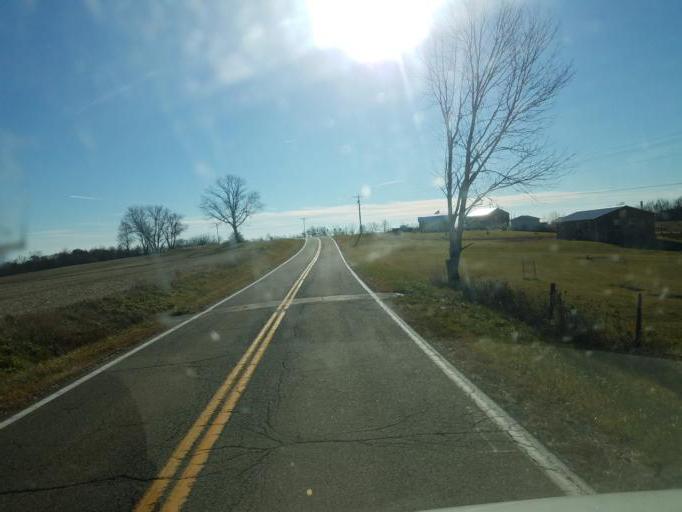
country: US
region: Ohio
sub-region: Knox County
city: Oak Hill
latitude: 40.2840
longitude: -82.1423
